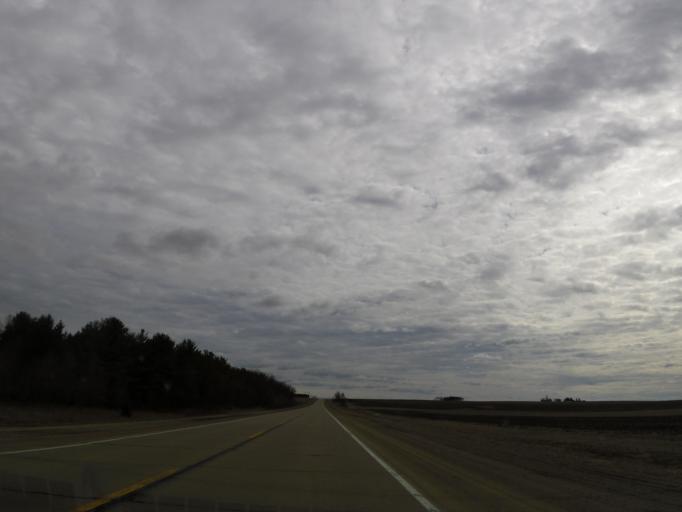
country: US
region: Iowa
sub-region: Howard County
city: Cresco
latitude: 43.3898
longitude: -92.2982
